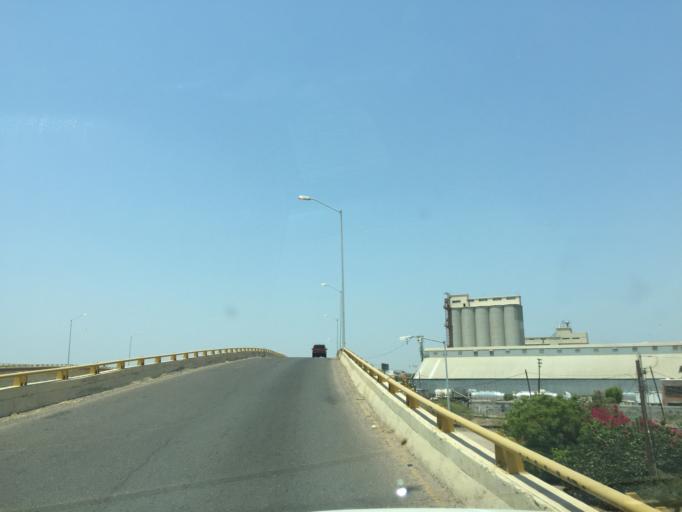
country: MX
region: Sonora
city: Navojoa
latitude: 27.0677
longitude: -109.4388
